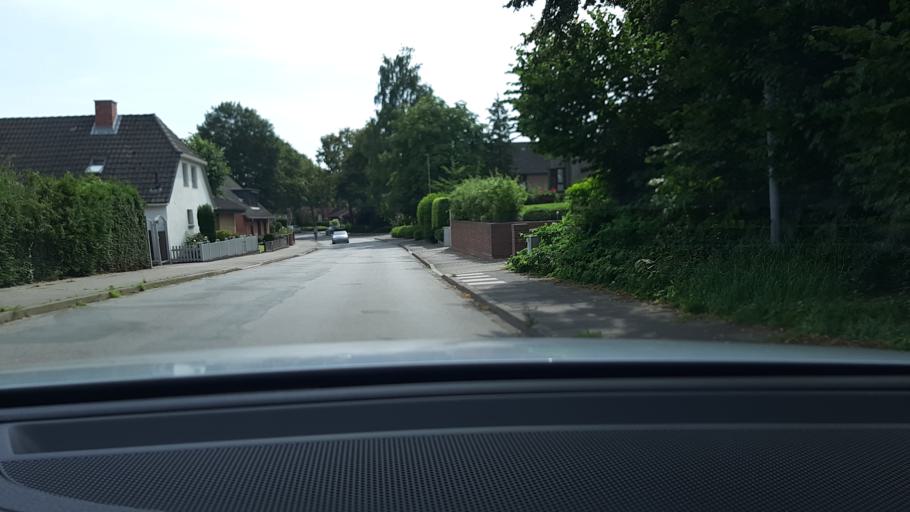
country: DE
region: Schleswig-Holstein
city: Reinfeld
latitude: 53.8349
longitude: 10.4789
